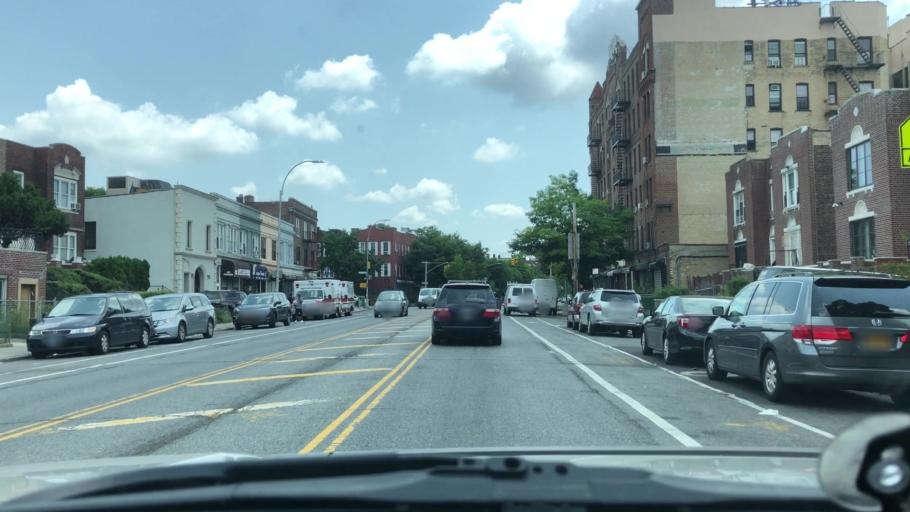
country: US
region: New York
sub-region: Kings County
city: Brooklyn
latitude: 40.6642
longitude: -73.9467
